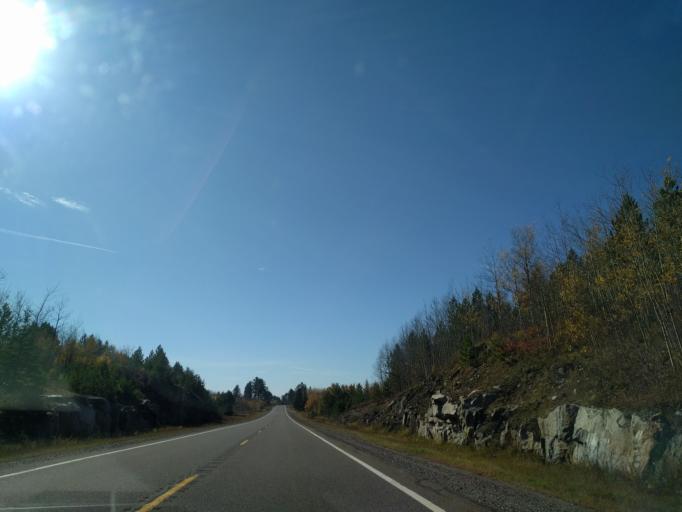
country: US
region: Michigan
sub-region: Marquette County
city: West Ishpeming
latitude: 46.4534
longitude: -87.9472
